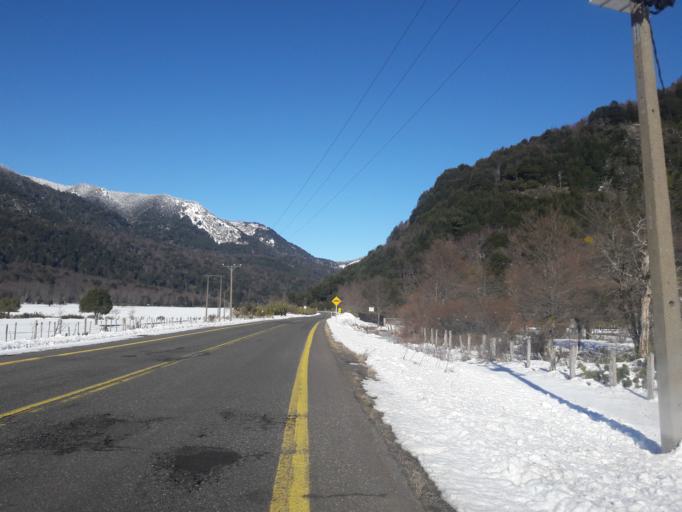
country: CL
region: Araucania
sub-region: Provincia de Cautin
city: Vilcun
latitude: -38.4860
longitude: -71.5302
